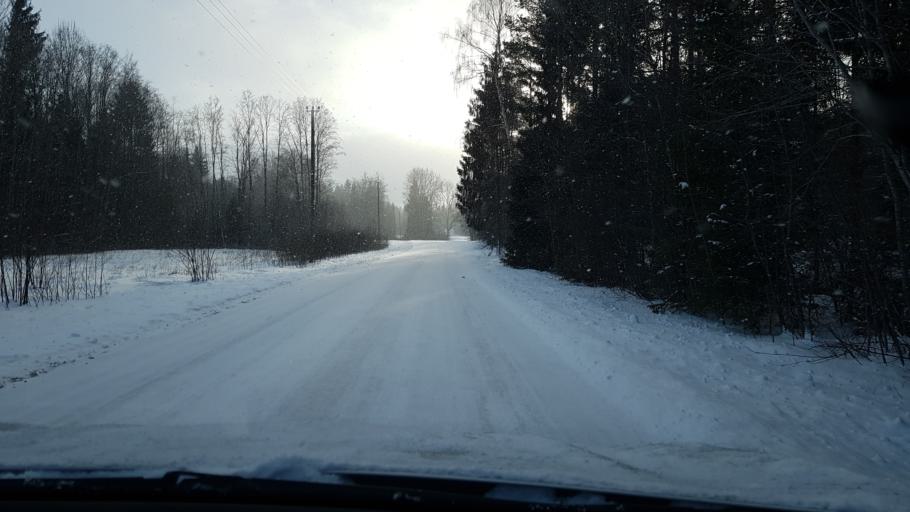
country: EE
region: Harju
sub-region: Nissi vald
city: Turba
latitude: 59.1901
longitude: 24.1395
